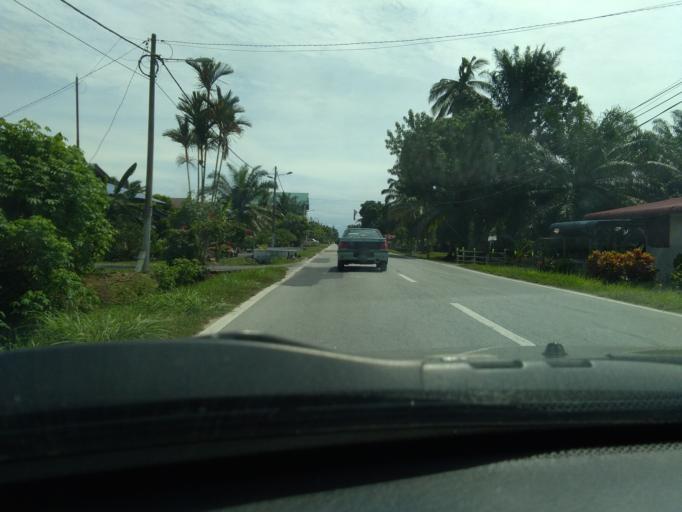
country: MY
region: Perak
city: Bagan Serai
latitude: 5.0245
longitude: 100.5525
